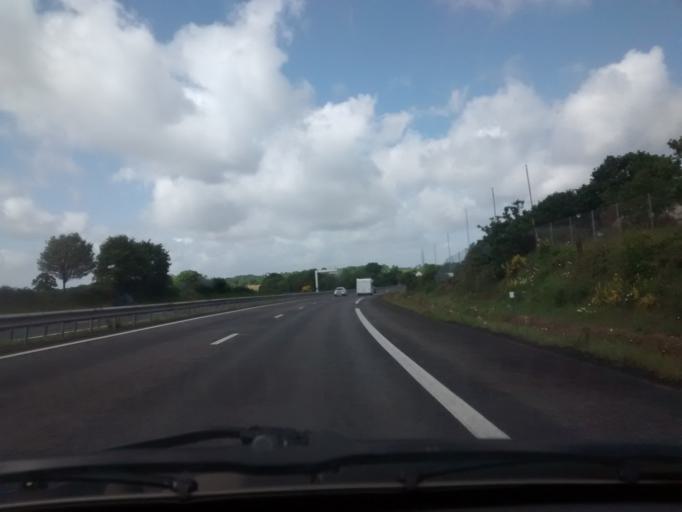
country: FR
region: Brittany
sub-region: Departement d'Ille-et-Vilaine
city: Saint-Thurial
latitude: 48.0456
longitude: -1.9301
